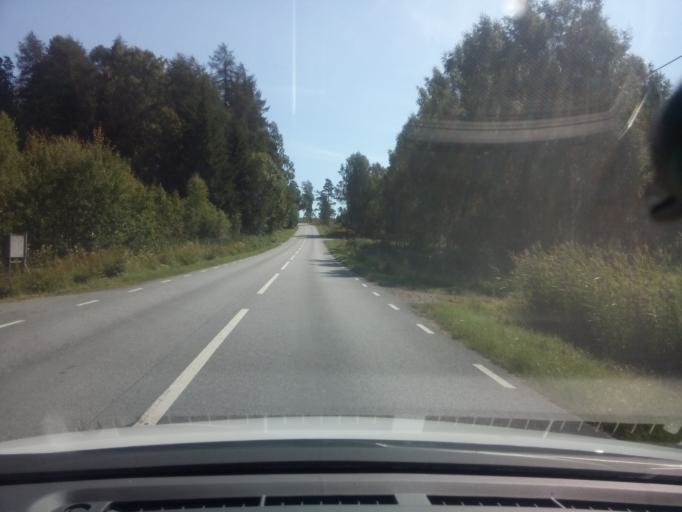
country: SE
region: Soedermanland
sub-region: Oxelosunds Kommun
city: Oxelosund
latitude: 58.7415
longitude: 17.1637
